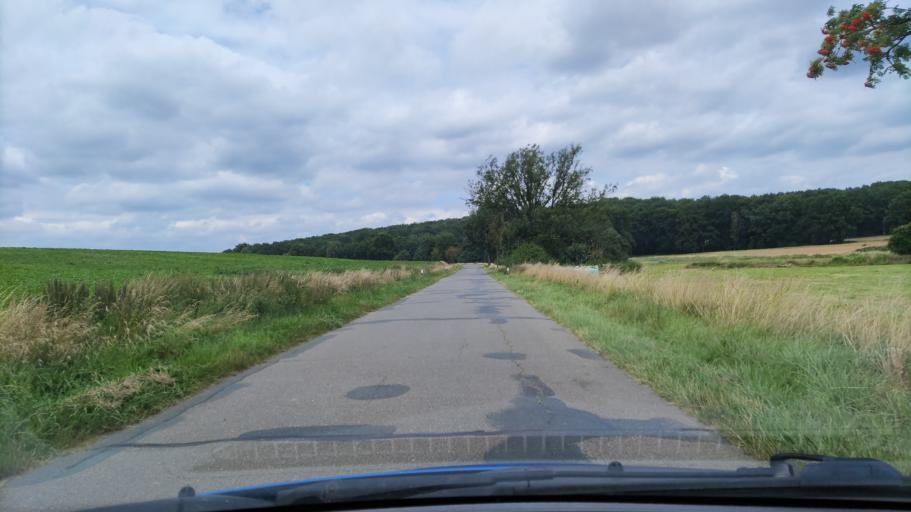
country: DE
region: Lower Saxony
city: Weste
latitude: 53.0764
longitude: 10.6894
